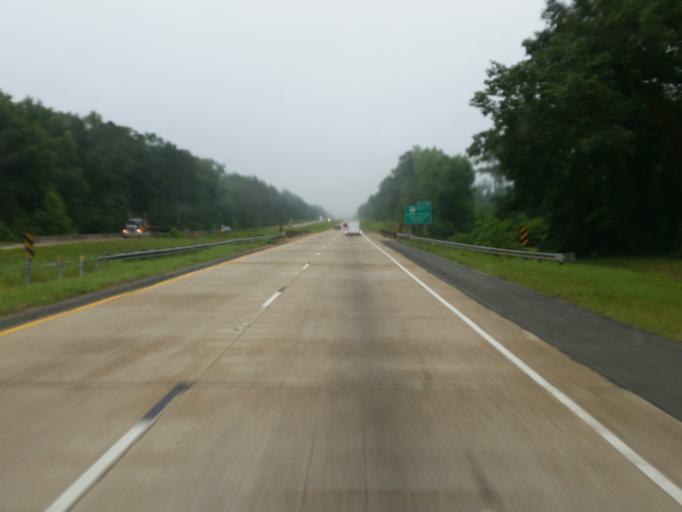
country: US
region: Louisiana
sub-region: Webster Parish
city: Sibley
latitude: 32.5841
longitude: -93.3768
